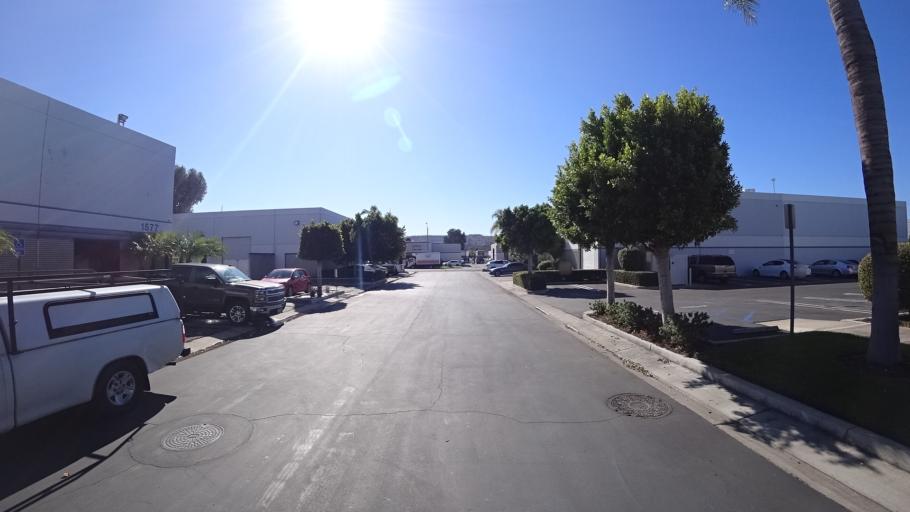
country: US
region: California
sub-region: Orange County
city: Yorba Linda
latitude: 33.8634
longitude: -117.8047
